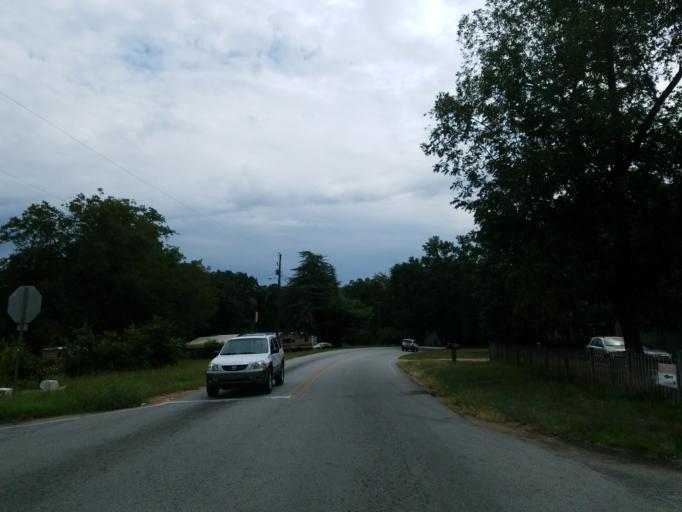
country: US
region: Georgia
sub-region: Spalding County
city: Experiment
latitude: 33.3193
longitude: -84.2859
